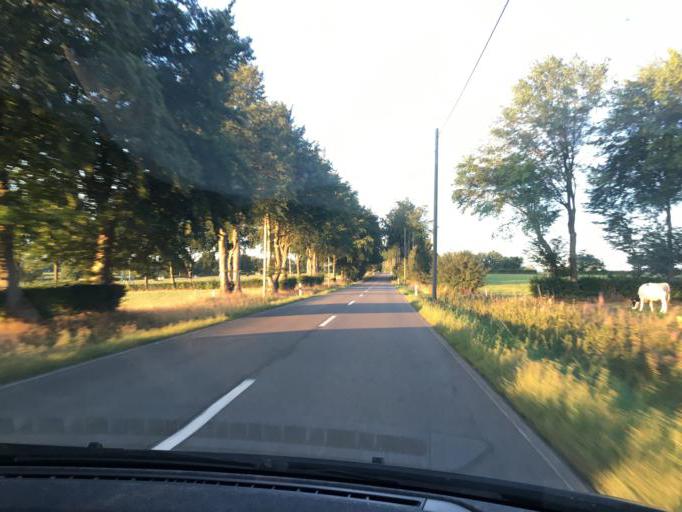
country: DE
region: North Rhine-Westphalia
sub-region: Regierungsbezirk Koln
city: Simmerath
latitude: 50.6425
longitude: 6.3225
